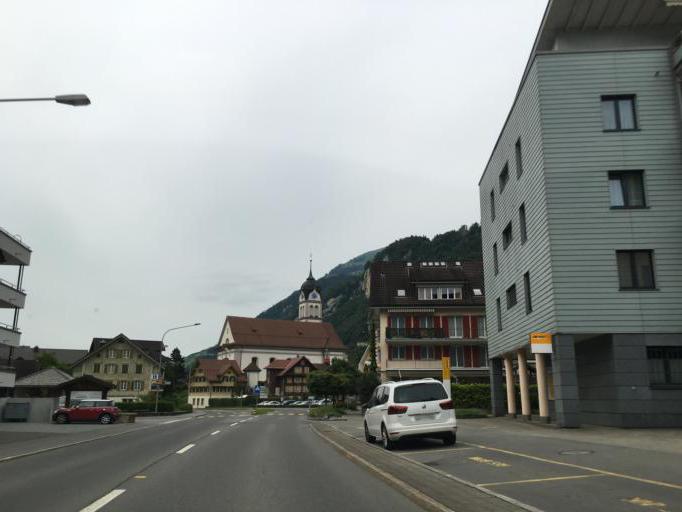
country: CH
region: Nidwalden
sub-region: Nidwalden
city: Wolfenschiessen
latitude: 46.9072
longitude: 8.3955
